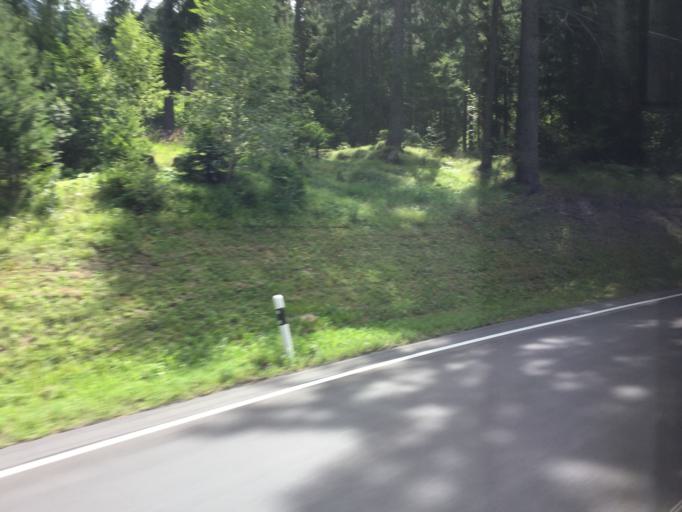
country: CH
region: Grisons
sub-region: Albula District
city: Tiefencastel
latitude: 46.6308
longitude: 9.5878
